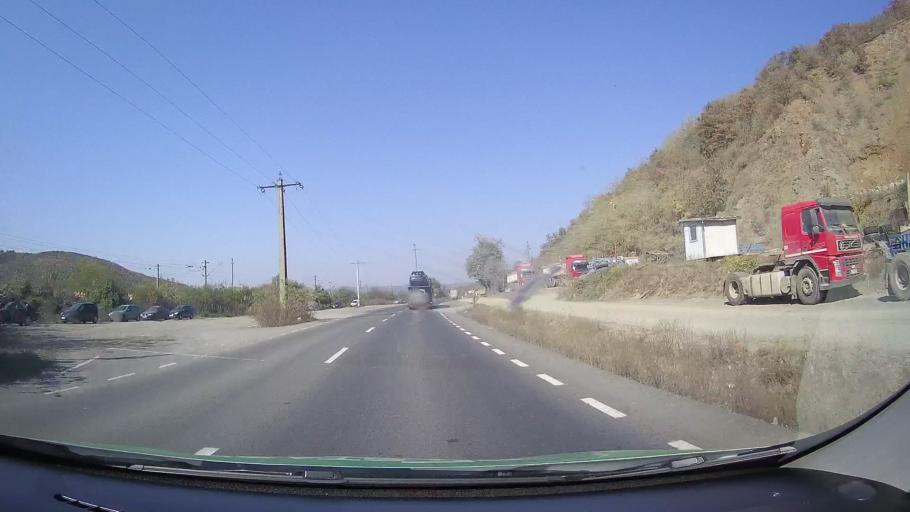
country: RO
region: Arad
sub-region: Comuna Bata
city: Bata
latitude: 46.0564
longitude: 22.0463
